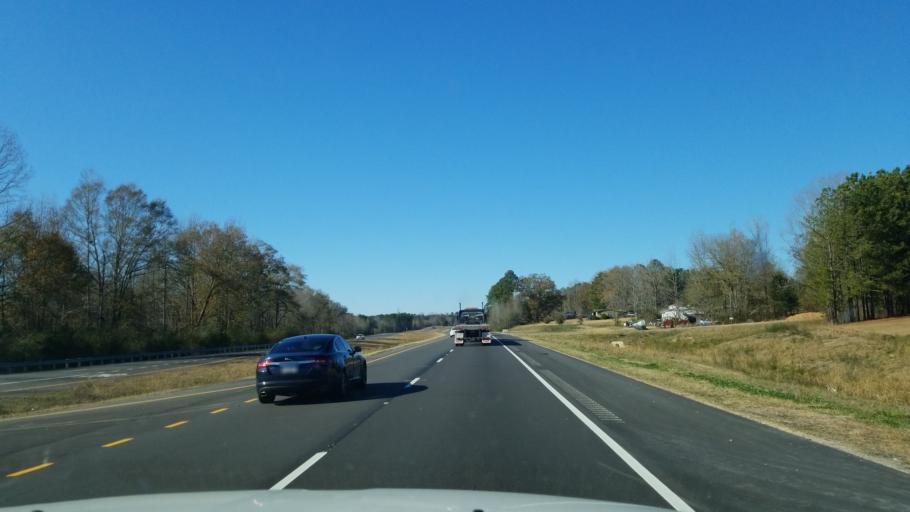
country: US
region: Alabama
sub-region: Pickens County
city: Gordo
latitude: 33.3488
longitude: -87.9536
